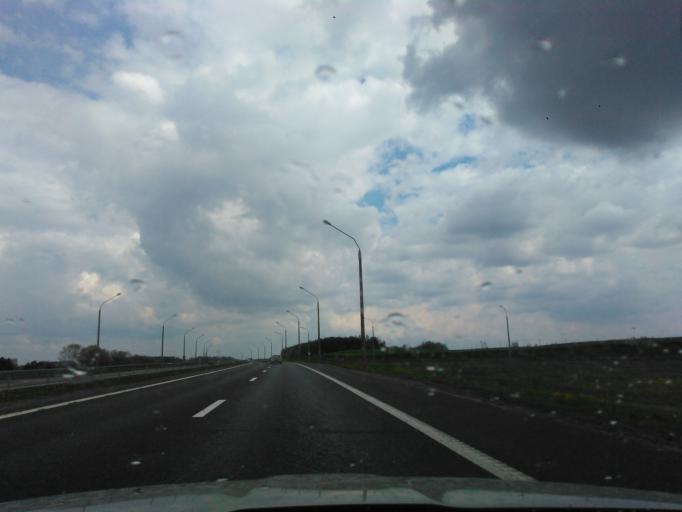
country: BY
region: Minsk
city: Slabada
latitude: 54.0161
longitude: 27.8947
